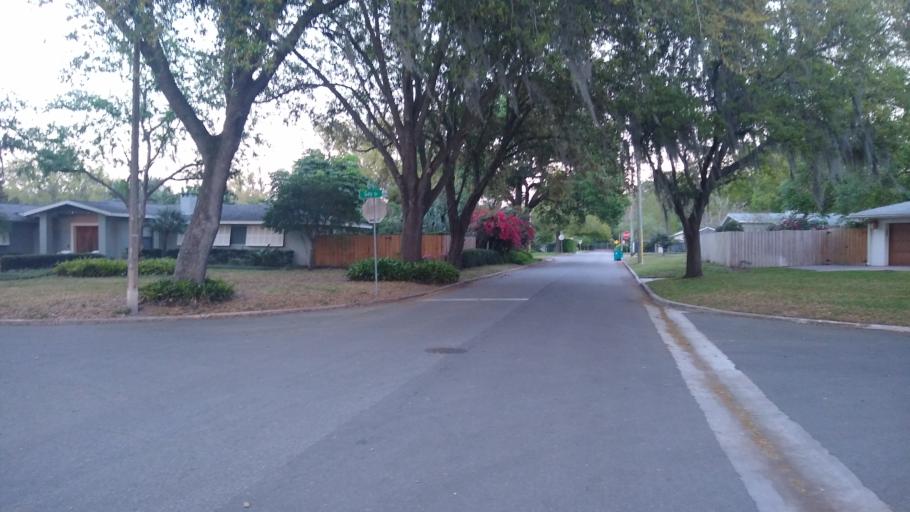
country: US
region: Florida
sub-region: Orange County
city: Orlando
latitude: 28.5667
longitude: -81.3621
